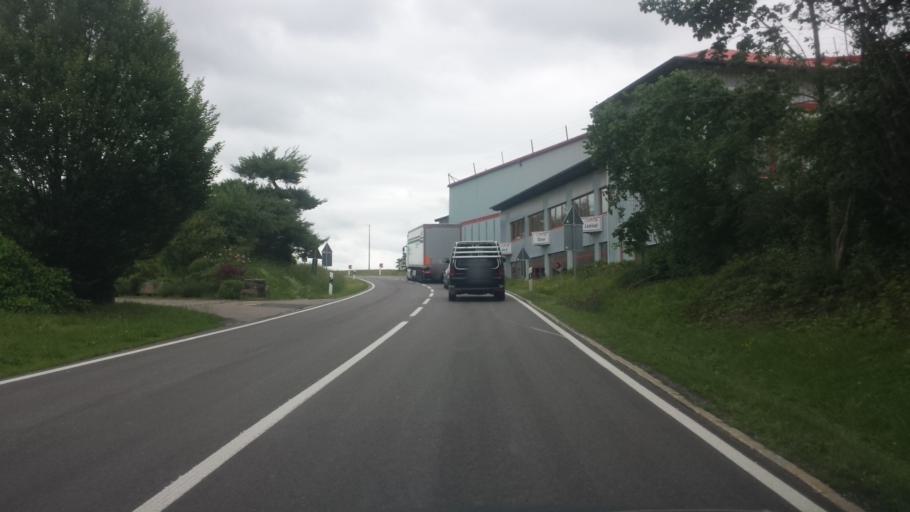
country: DE
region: Baden-Wuerttemberg
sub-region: Regierungsbezirk Stuttgart
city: Rot am See
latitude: 49.2602
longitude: 10.0148
